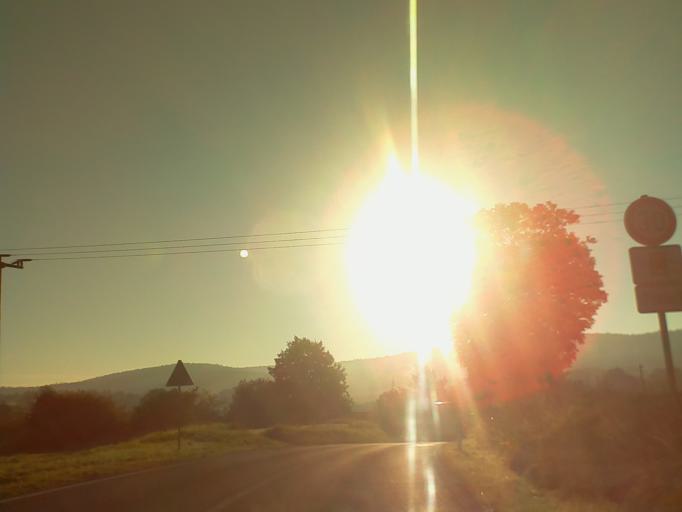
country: DE
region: Thuringia
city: Unterbodnitz
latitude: 50.8126
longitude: 11.6526
